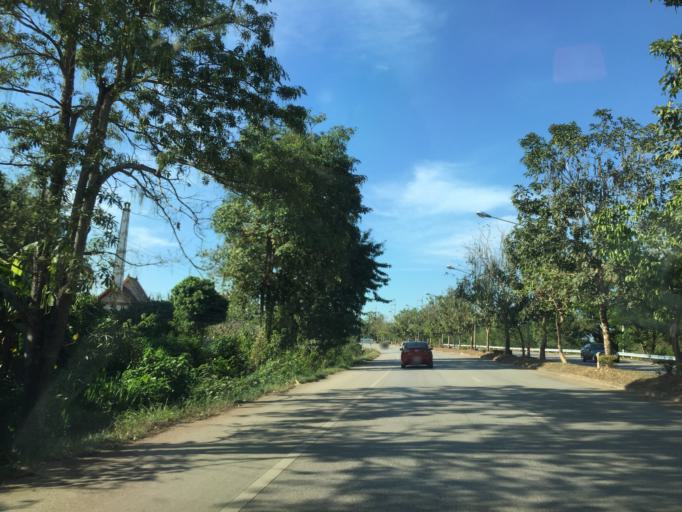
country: TH
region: Loei
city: Wang Saphung
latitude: 17.3147
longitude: 101.7707
